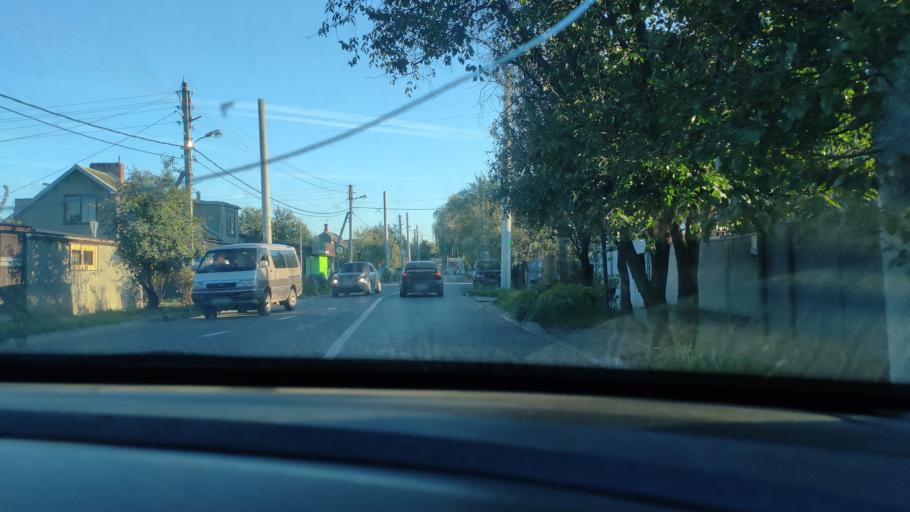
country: RU
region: Krasnodarskiy
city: Krasnodar
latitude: 45.0398
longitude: 38.9234
